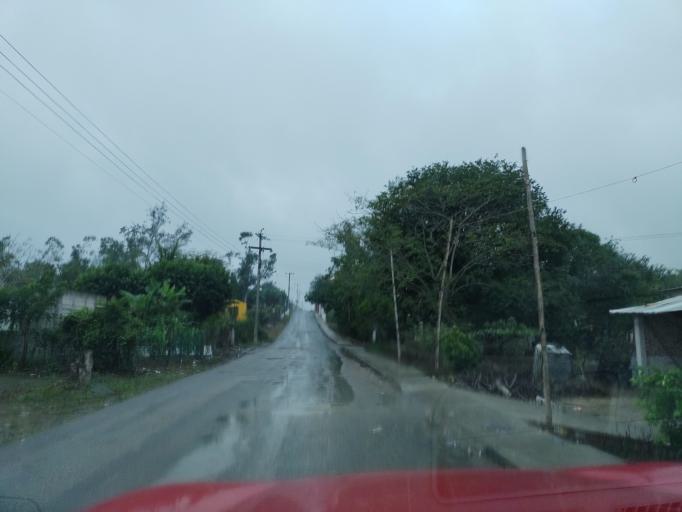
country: MX
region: Veracruz
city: Agua Dulce
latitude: 20.3336
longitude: -97.3244
